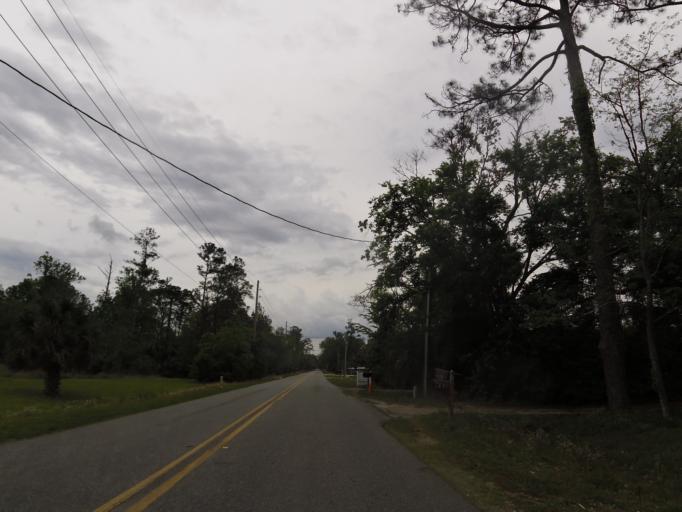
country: US
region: Florida
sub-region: Saint Johns County
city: Palm Valley
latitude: 30.2080
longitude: -81.4081
